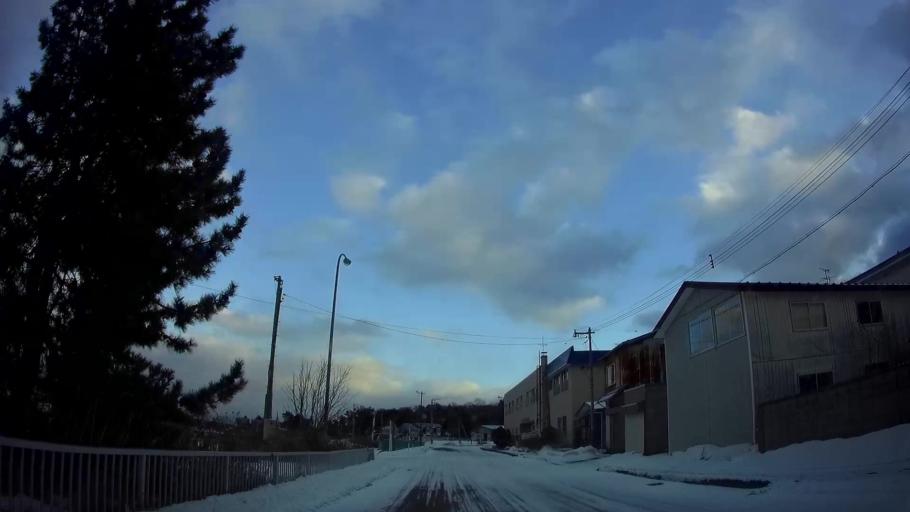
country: JP
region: Hokkaido
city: Nanae
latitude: 42.0302
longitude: 140.8266
